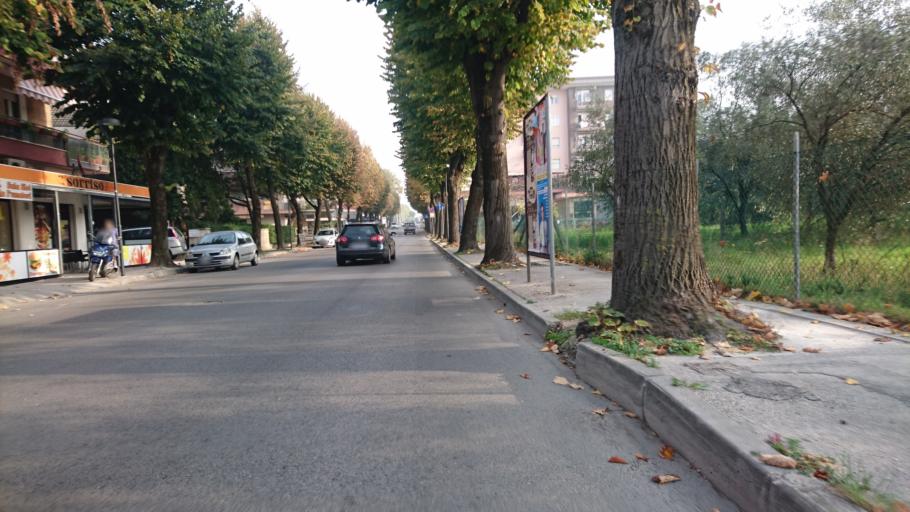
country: IT
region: Emilia-Romagna
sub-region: Provincia di Rimini
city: Rimini
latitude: 44.0748
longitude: 12.5582
